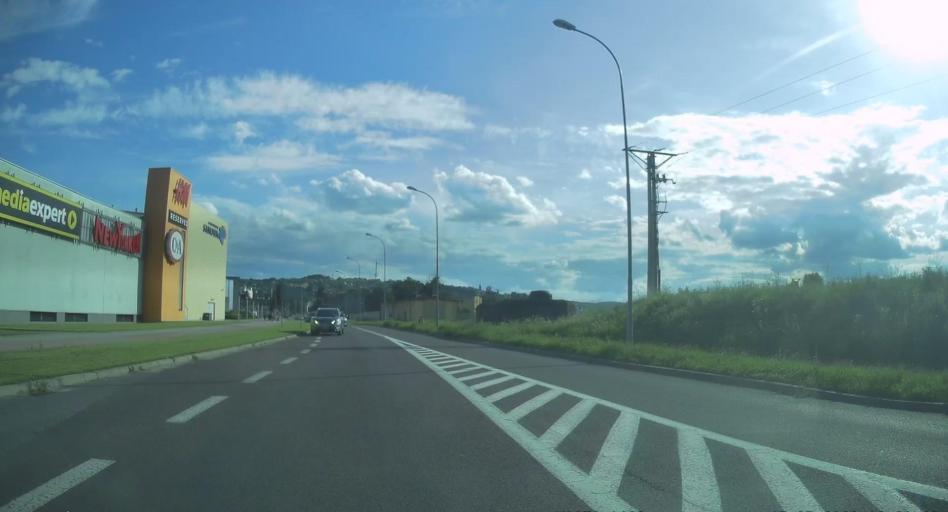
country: PL
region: Subcarpathian Voivodeship
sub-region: Przemysl
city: Przemysl
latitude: 49.7917
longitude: 22.7823
